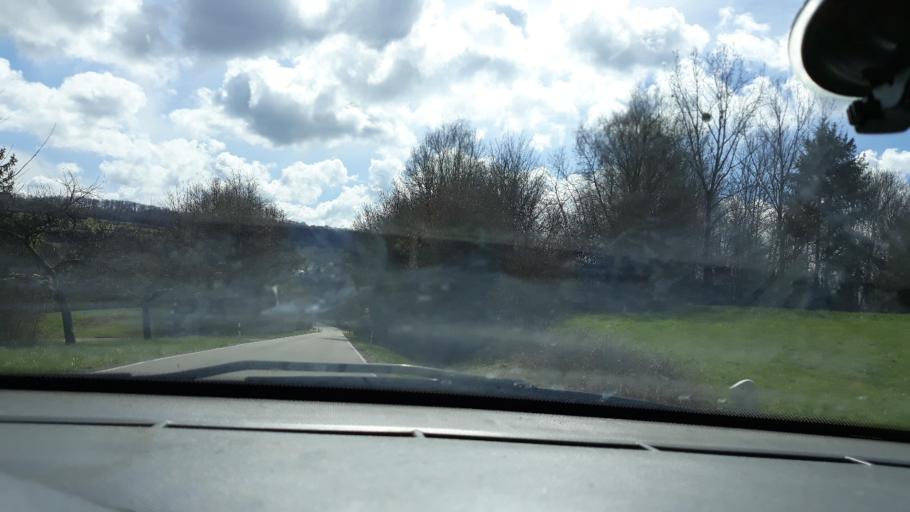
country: DE
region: Saarland
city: Gersheim
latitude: 49.1792
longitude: 7.2359
